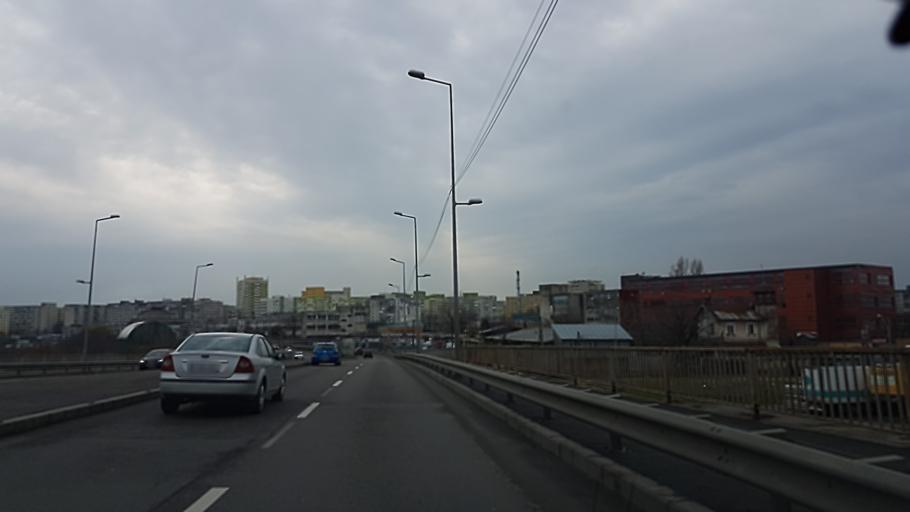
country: RO
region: Ilfov
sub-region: Comuna Fundeni-Dobroesti
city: Fundeni
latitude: 44.4492
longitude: 26.1533
